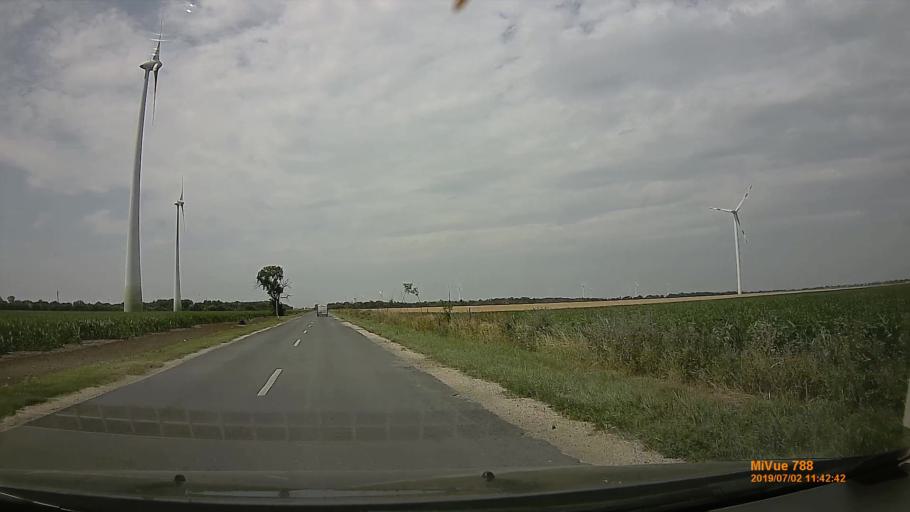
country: HU
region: Gyor-Moson-Sopron
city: Mosonmagyarovar
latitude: 47.8792
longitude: 17.2287
